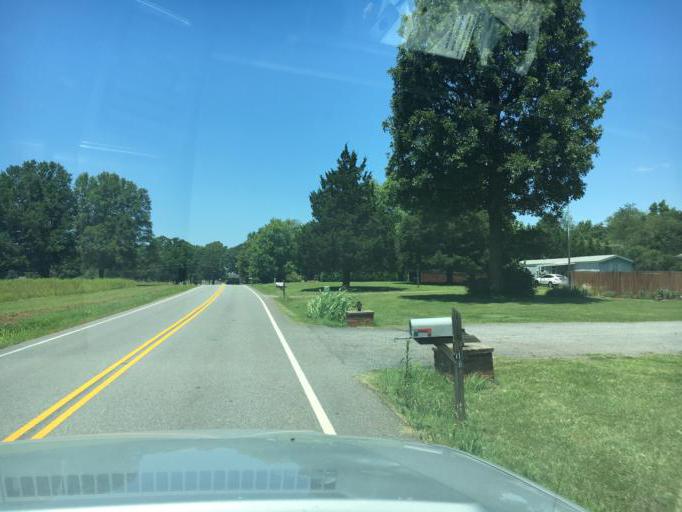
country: US
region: South Carolina
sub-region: Spartanburg County
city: Fairforest
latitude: 34.9747
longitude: -82.0541
